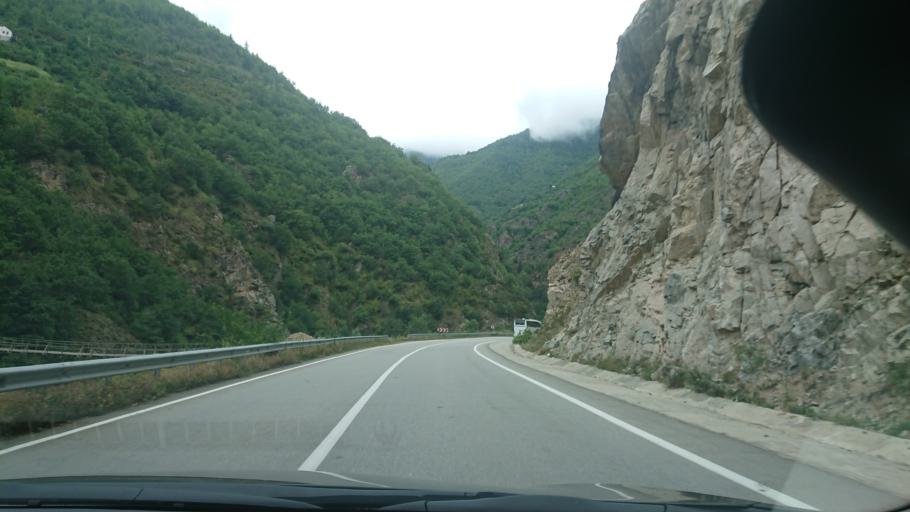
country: TR
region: Gumushane
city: Kurtun
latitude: 40.7056
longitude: 39.0686
